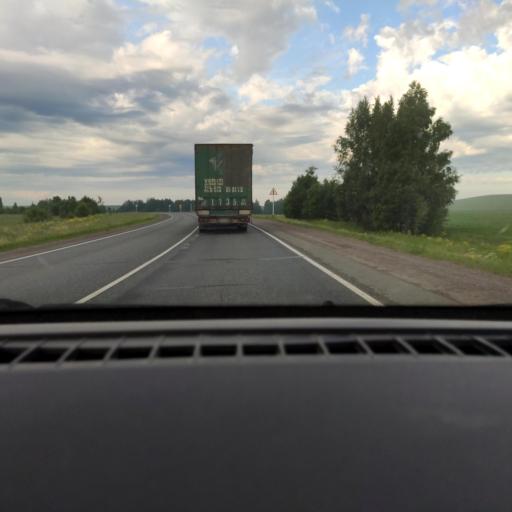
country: RU
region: Perm
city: Chastyye
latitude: 57.3945
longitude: 54.4375
